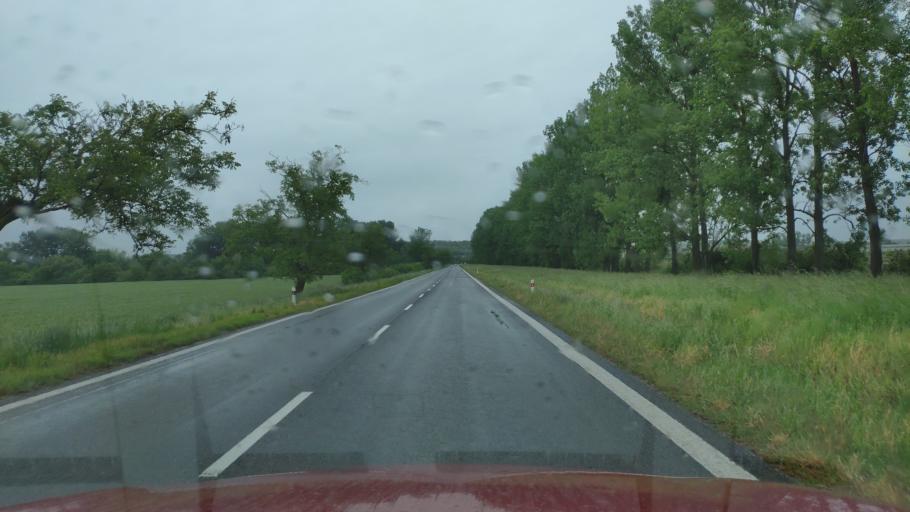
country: HU
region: Borsod-Abauj-Zemplen
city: Ricse
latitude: 48.4324
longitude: 21.9036
